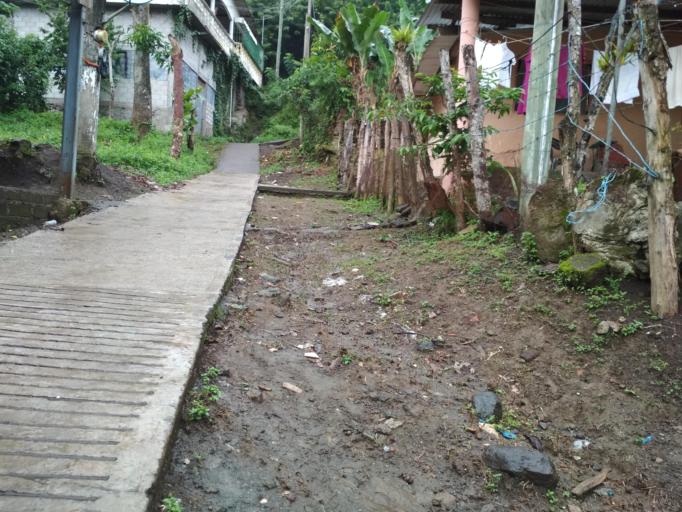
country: MX
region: Veracruz
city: San Andres Tuxtla
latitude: 18.4504
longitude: -95.1988
